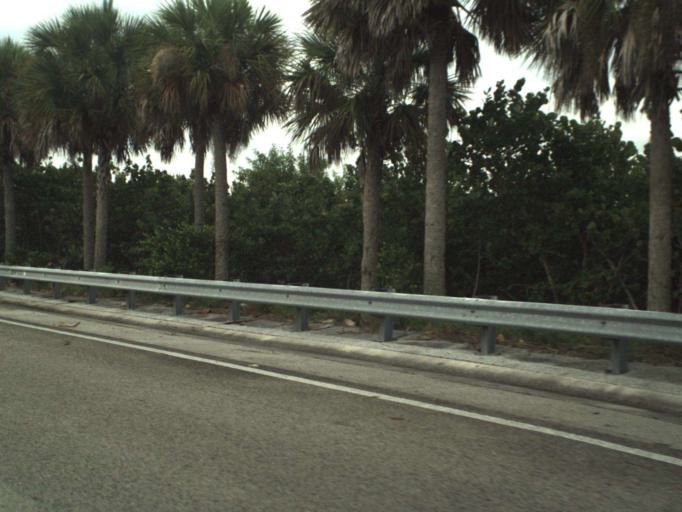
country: US
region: Florida
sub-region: Martin County
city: Palm City
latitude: 27.1212
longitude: -80.2723
